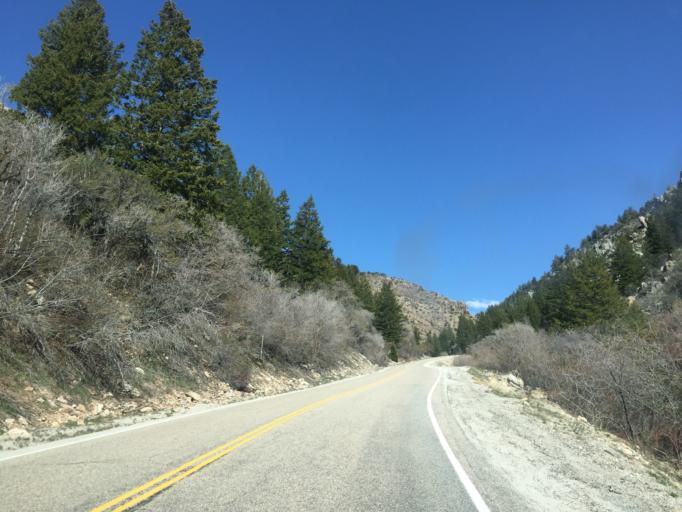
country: US
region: Utah
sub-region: Weber County
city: Wolf Creek
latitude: 41.3550
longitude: -111.7971
